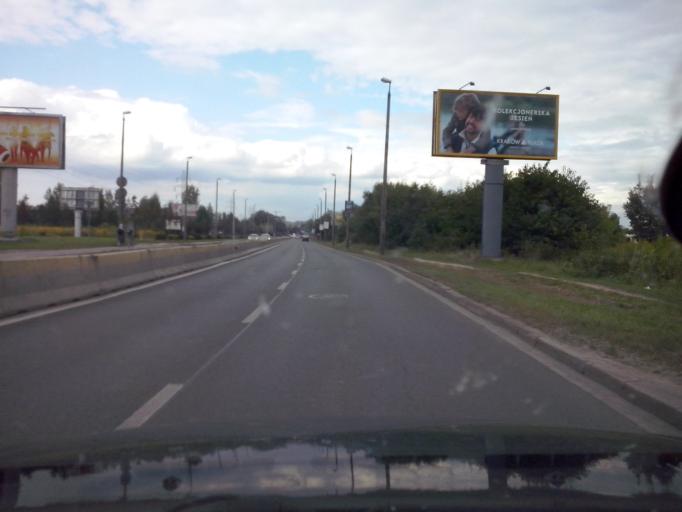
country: PL
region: Lesser Poland Voivodeship
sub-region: Krakow
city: Krakow
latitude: 50.0589
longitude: 20.0031
